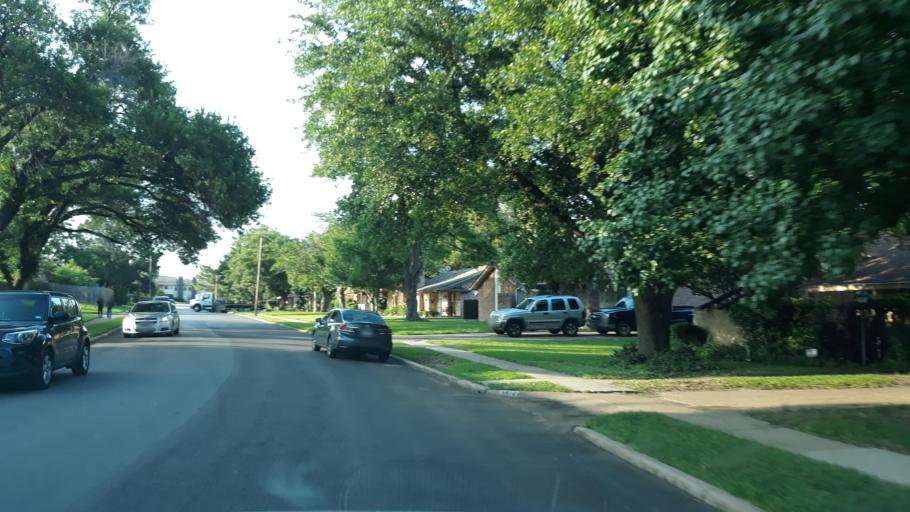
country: US
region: Texas
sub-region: Dallas County
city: Irving
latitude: 32.8550
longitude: -96.9986
